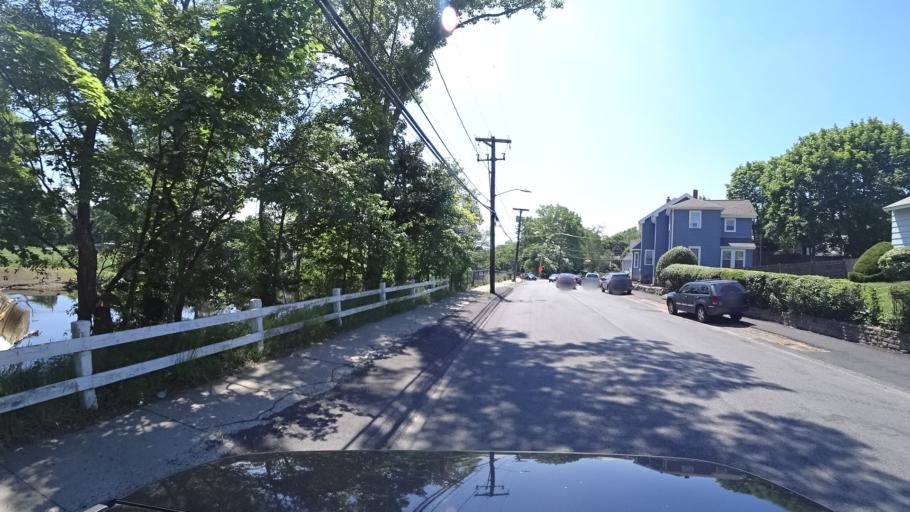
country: US
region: Massachusetts
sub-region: Norfolk County
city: Dedham
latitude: 42.2512
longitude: -71.1546
